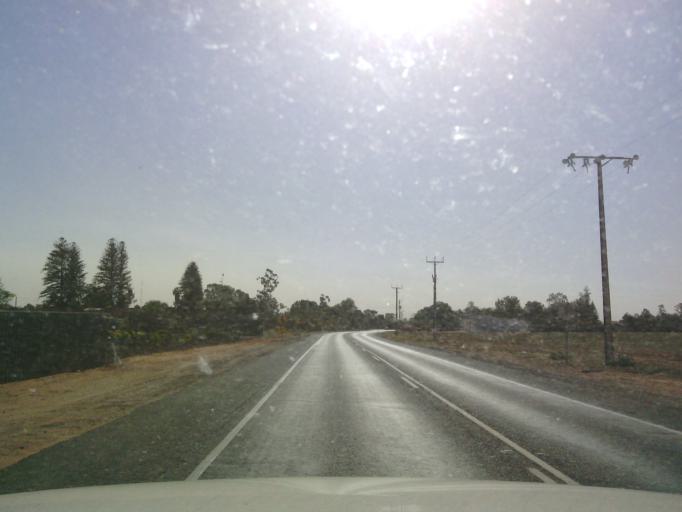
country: AU
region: South Australia
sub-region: Berri and Barmera
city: Berri
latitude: -34.2821
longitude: 140.5882
